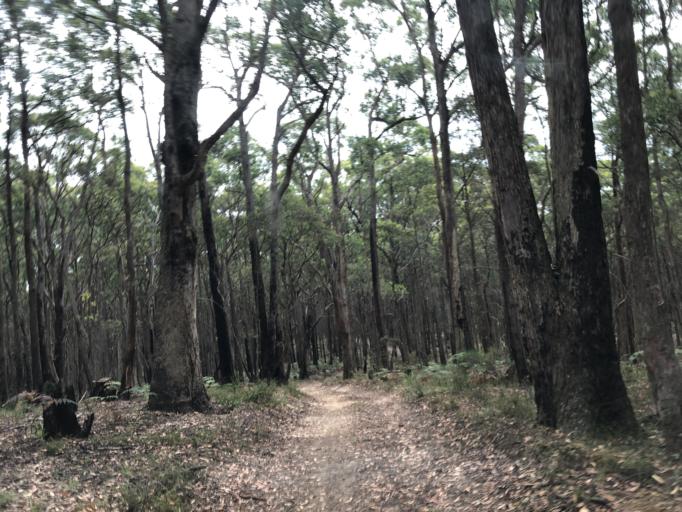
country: AU
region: Victoria
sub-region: Moorabool
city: Bacchus Marsh
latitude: -37.4380
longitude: 144.3449
